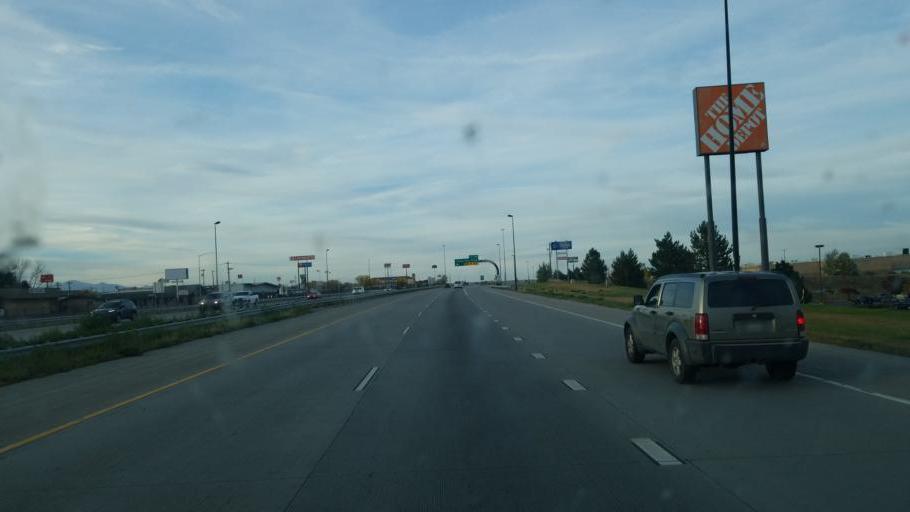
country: US
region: Colorado
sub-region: Pueblo County
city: Pueblo
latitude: 38.3147
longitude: -104.6150
